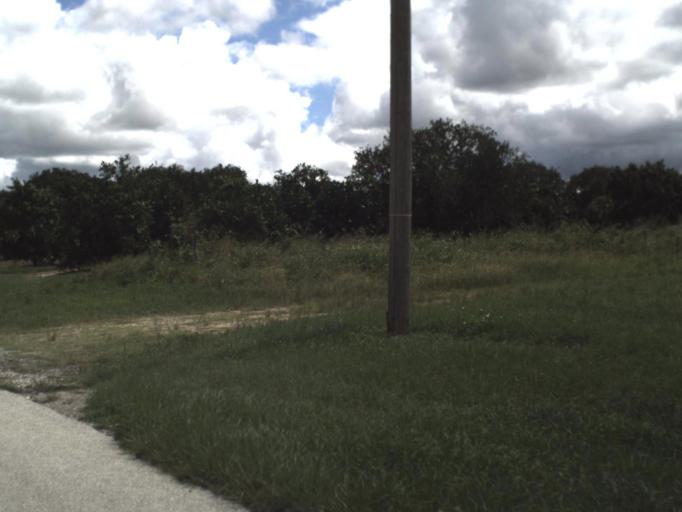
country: US
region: Florida
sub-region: Polk County
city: Fort Meade
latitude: 27.7335
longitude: -81.7200
